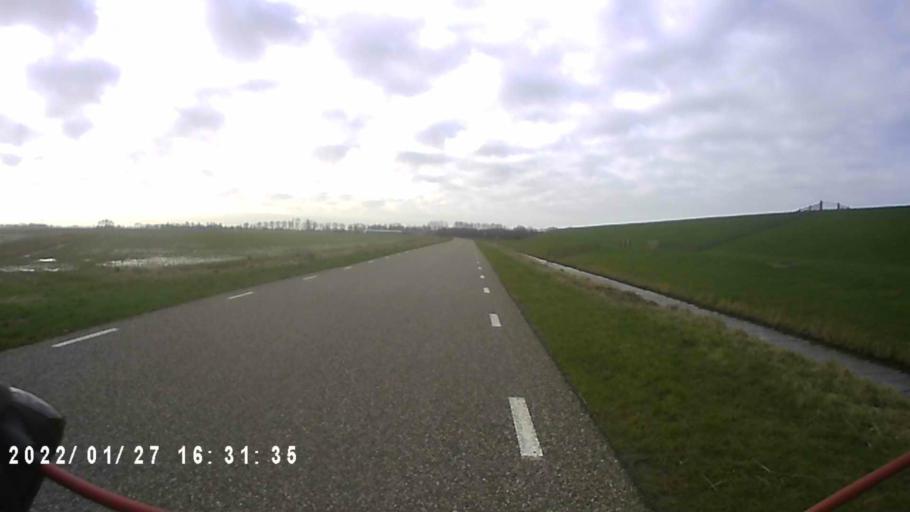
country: NL
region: Friesland
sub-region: Gemeente Dongeradeel
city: Ternaard
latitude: 53.4014
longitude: 6.0284
